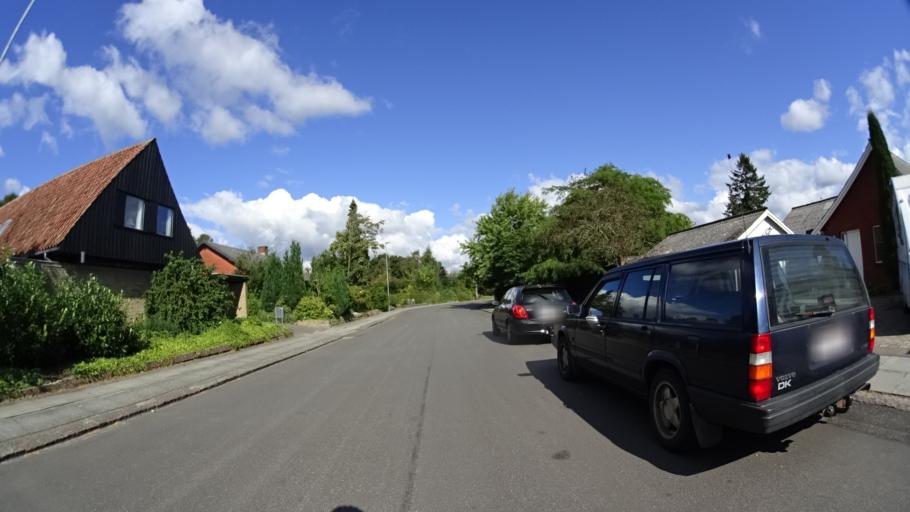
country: DK
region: Central Jutland
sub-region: Arhus Kommune
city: Arhus
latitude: 56.1156
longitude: 10.1813
